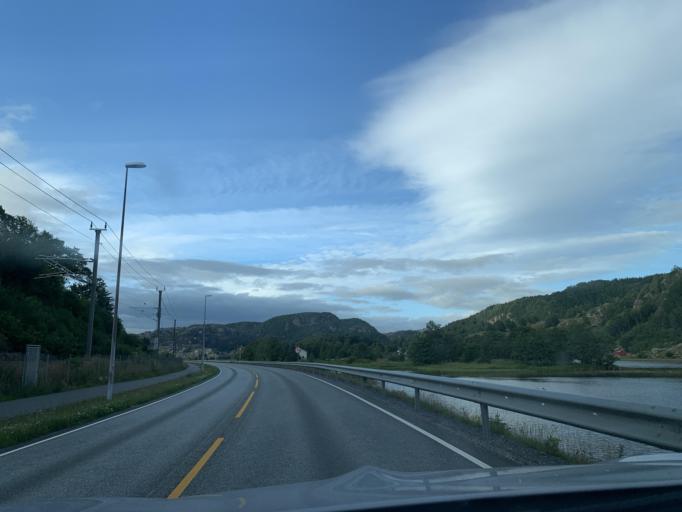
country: NO
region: Rogaland
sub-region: Eigersund
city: Egersund
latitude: 58.4643
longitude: 6.0224
